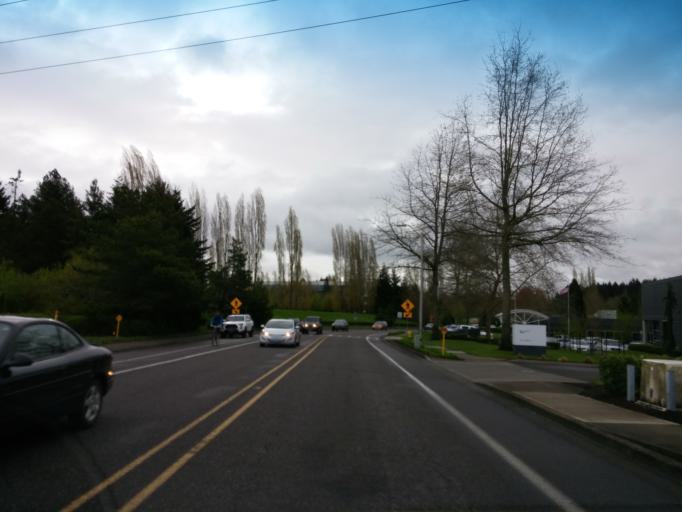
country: US
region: Oregon
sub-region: Washington County
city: Cedar Mill
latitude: 45.5088
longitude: -122.8355
